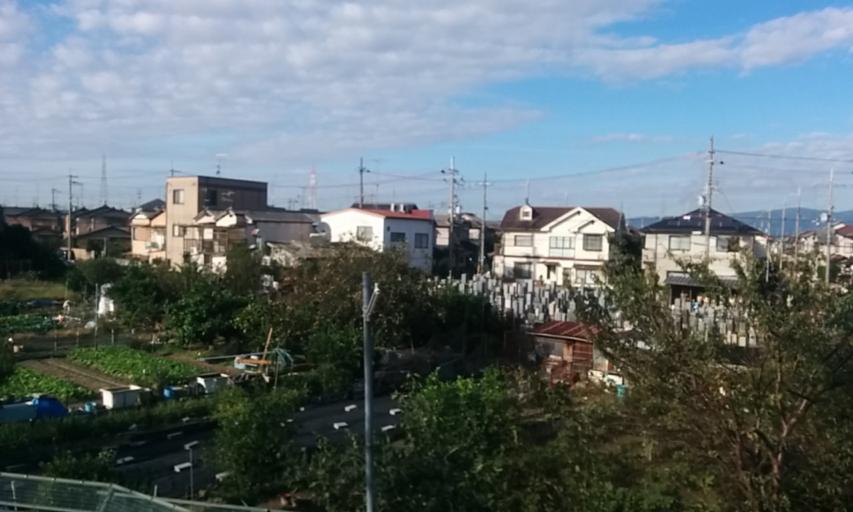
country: JP
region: Kyoto
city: Uji
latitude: 34.9227
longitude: 135.7668
